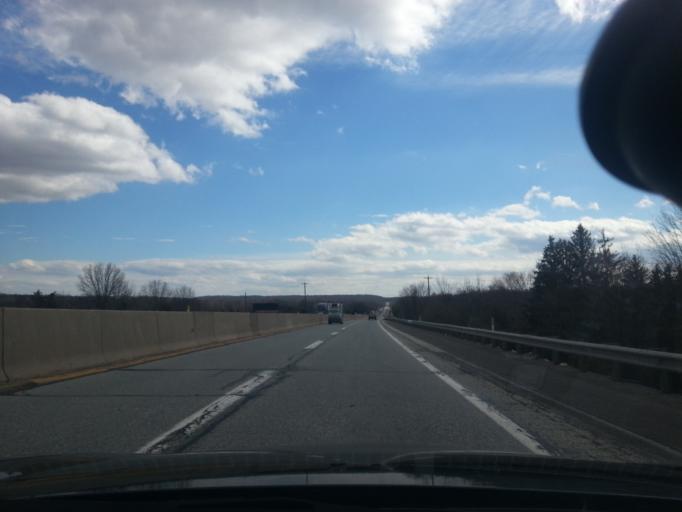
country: US
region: Pennsylvania
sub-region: Bucks County
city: Spinnerstown
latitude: 40.4197
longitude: -75.4152
